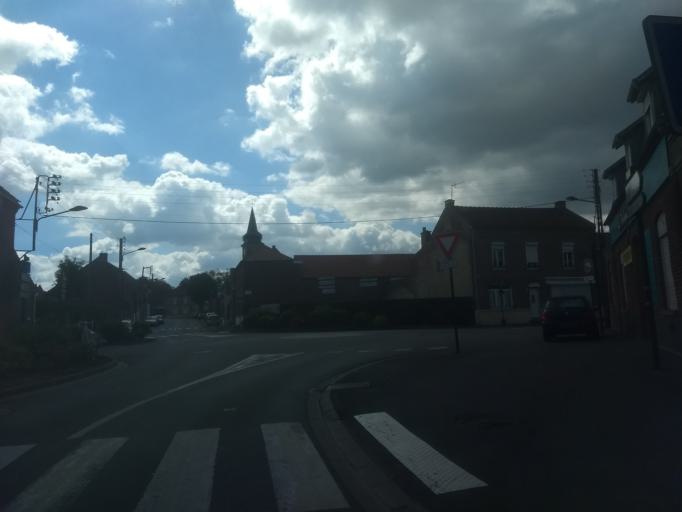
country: FR
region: Nord-Pas-de-Calais
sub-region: Departement du Pas-de-Calais
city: Bailleul-Sir-Berthoult
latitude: 50.3395
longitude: 2.8511
